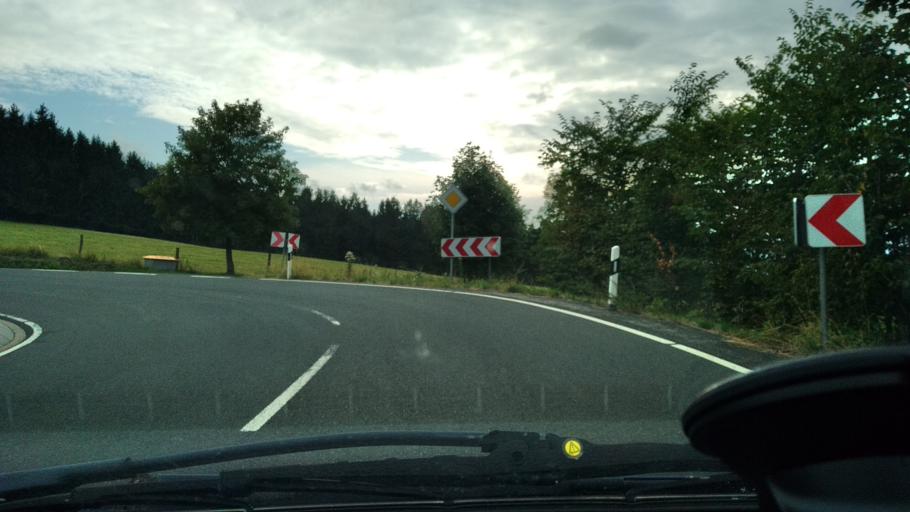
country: DE
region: Hesse
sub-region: Regierungsbezirk Giessen
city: Haiger
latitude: 50.8483
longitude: 8.2105
